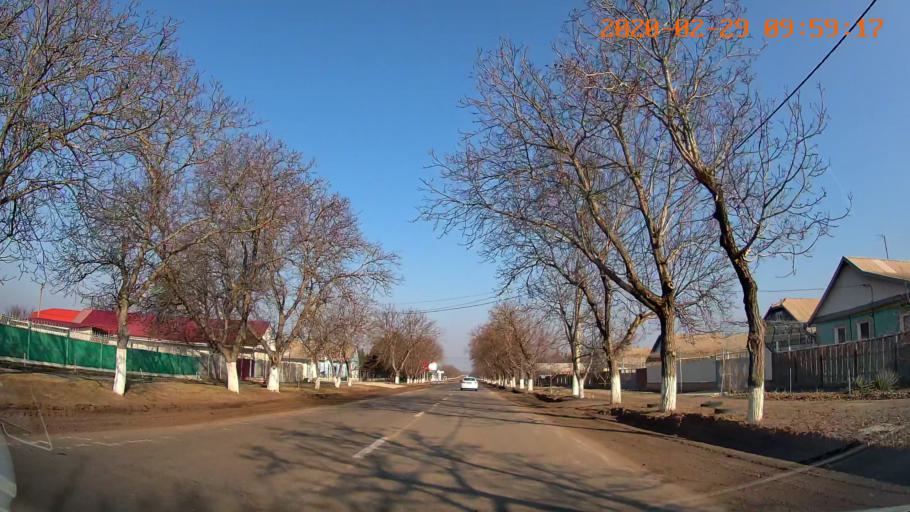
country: MD
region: Telenesti
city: Slobozia
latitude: 46.7555
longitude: 29.6887
